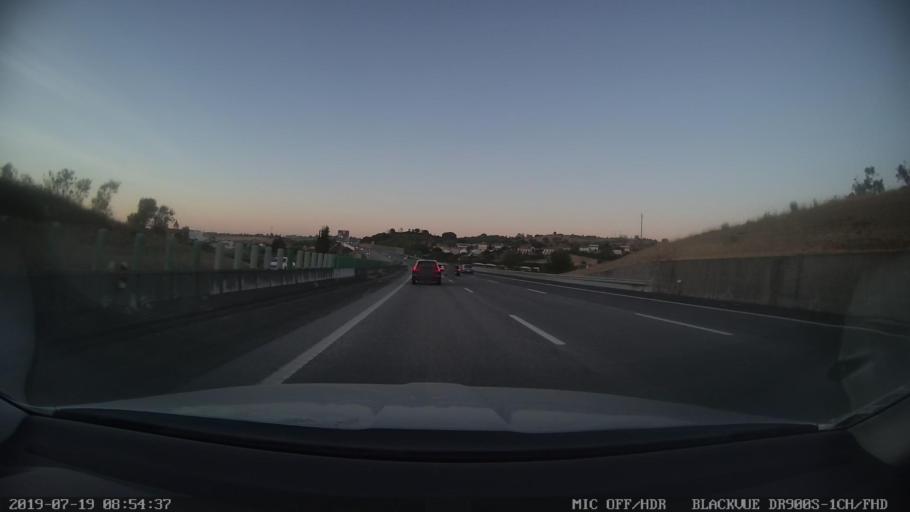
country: PT
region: Lisbon
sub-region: Azambuja
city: Aveiras de Cima
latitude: 39.1303
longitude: -8.8984
